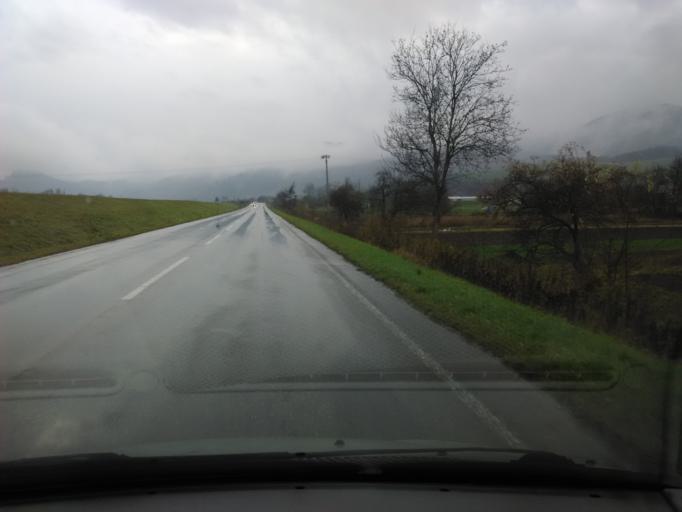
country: SK
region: Trenciansky
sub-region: Okres Povazska Bystrica
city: Povazska Bystrica
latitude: 49.1677
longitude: 18.4741
